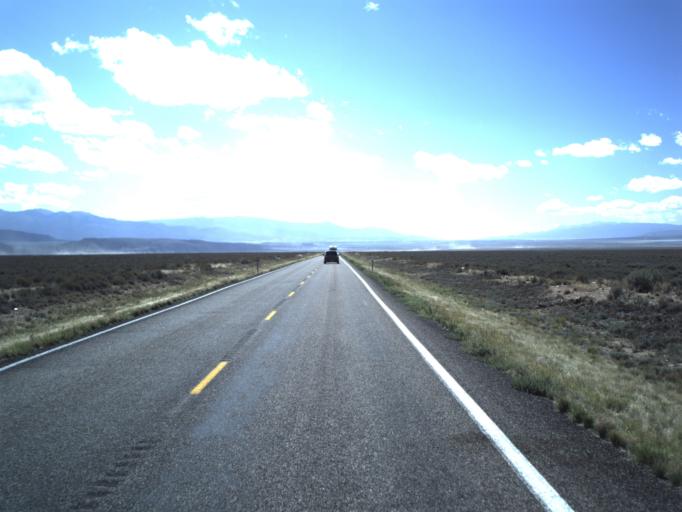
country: US
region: Utah
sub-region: Iron County
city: Enoch
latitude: 37.9835
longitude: -113.0027
